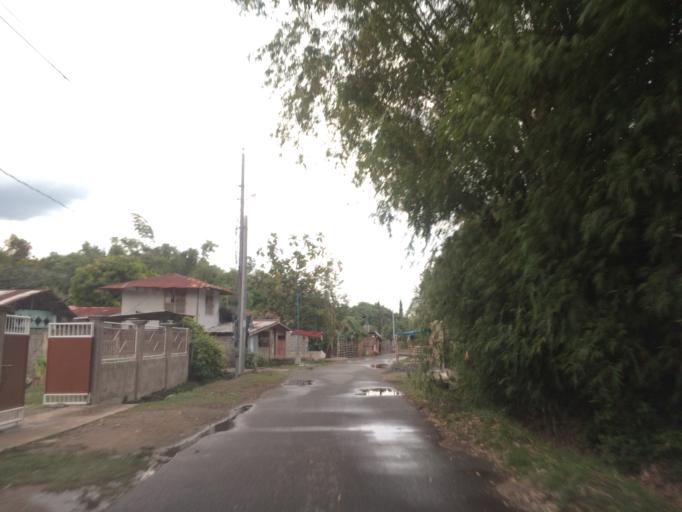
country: PH
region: Ilocos
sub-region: Province of Pangasinan
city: Anambongan
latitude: 15.8723
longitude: 120.3872
